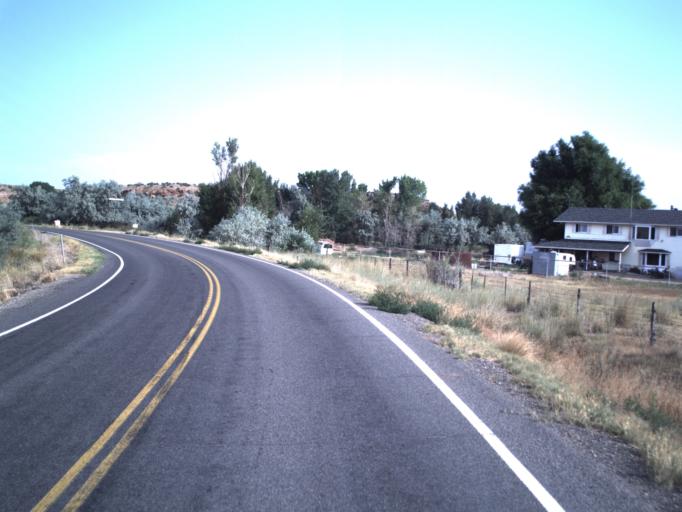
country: US
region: Utah
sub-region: Duchesne County
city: Duchesne
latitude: 40.2846
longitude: -110.2191
